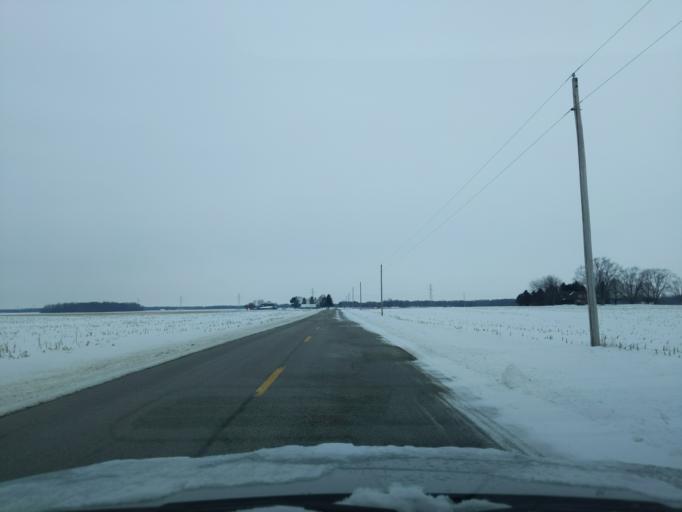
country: US
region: Indiana
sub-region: Benton County
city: Otterbein
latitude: 40.4168
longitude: -87.0750
